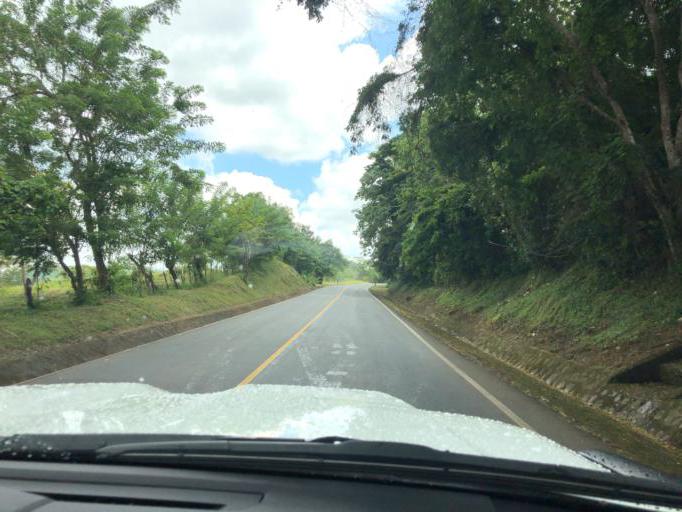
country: NI
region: Chontales
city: Villa Sandino
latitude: 11.9968
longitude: -84.9233
